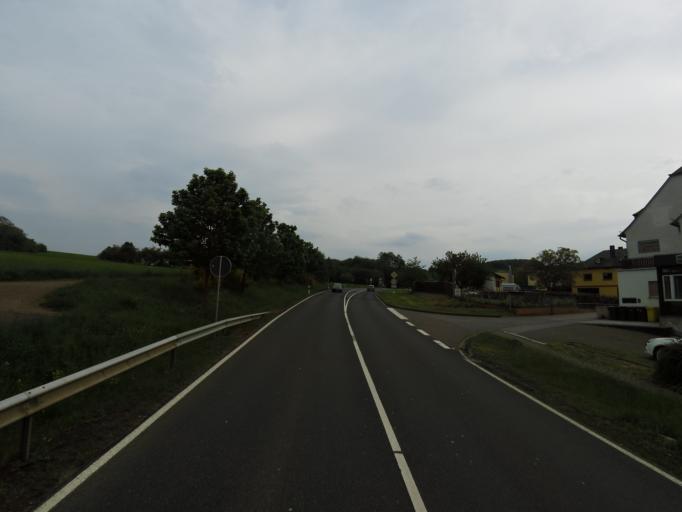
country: DE
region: Rheinland-Pfalz
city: Waldesch
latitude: 50.2804
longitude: 7.5499
